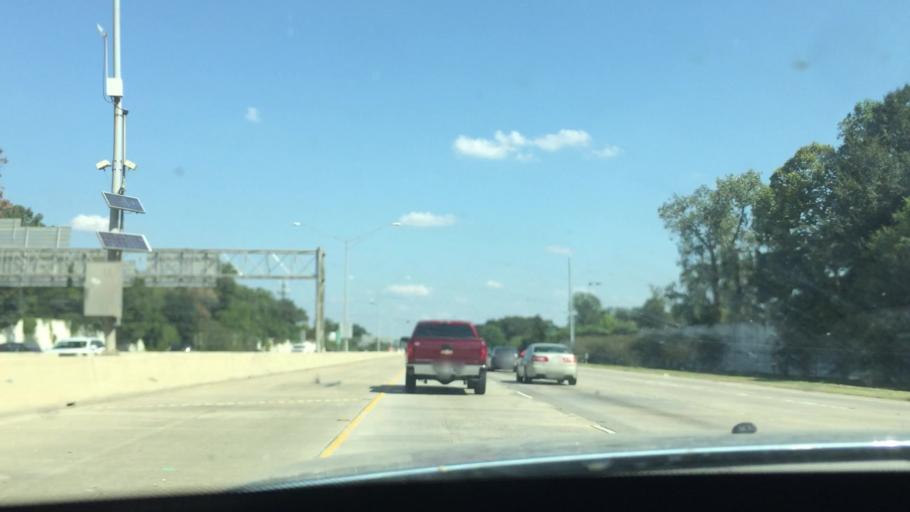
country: US
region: Louisiana
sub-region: East Baton Rouge Parish
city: Westminster
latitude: 30.4182
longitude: -91.1086
